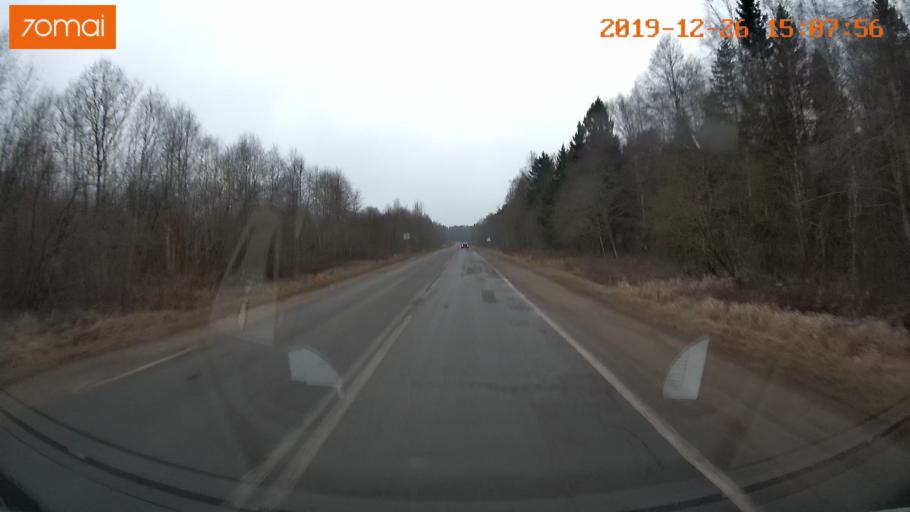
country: RU
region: Jaroslavl
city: Rybinsk
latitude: 58.1650
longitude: 38.8417
